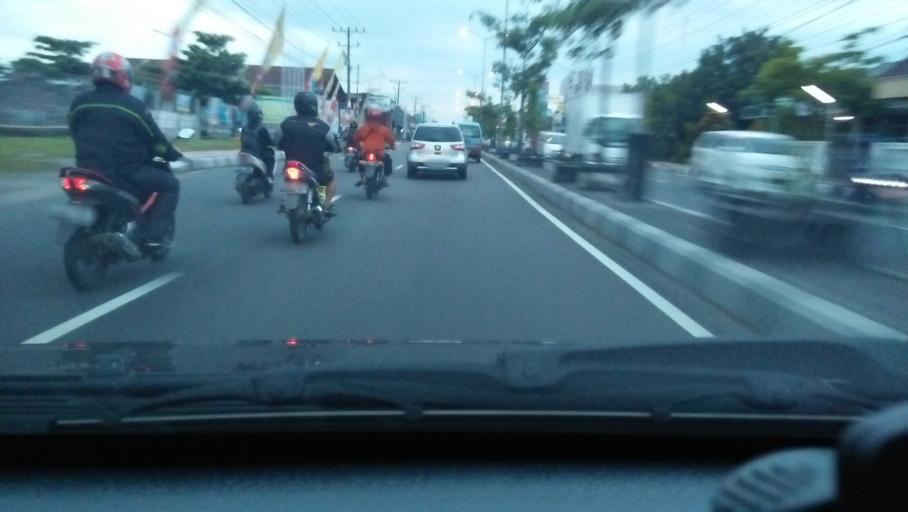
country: ID
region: Central Java
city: Mertoyudan
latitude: -7.5139
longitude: 110.2256
